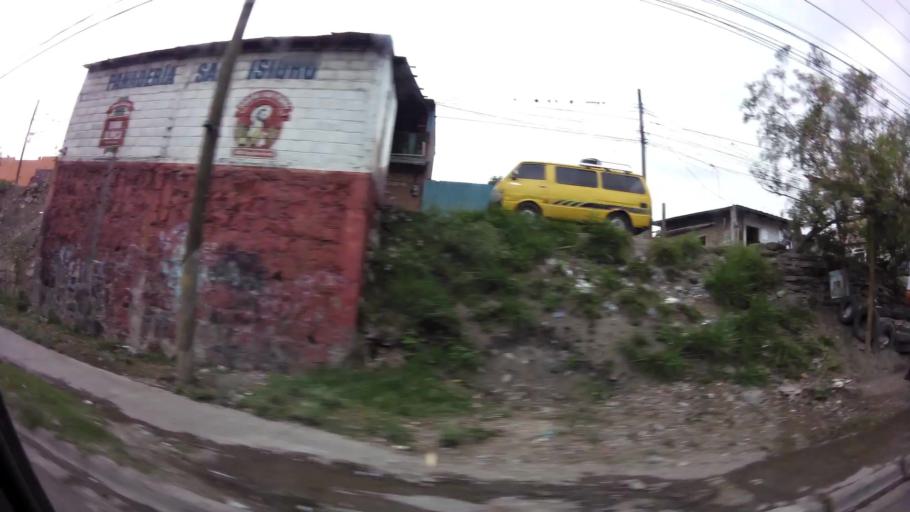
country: HN
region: Francisco Morazan
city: El Lolo
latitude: 14.1012
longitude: -87.2411
